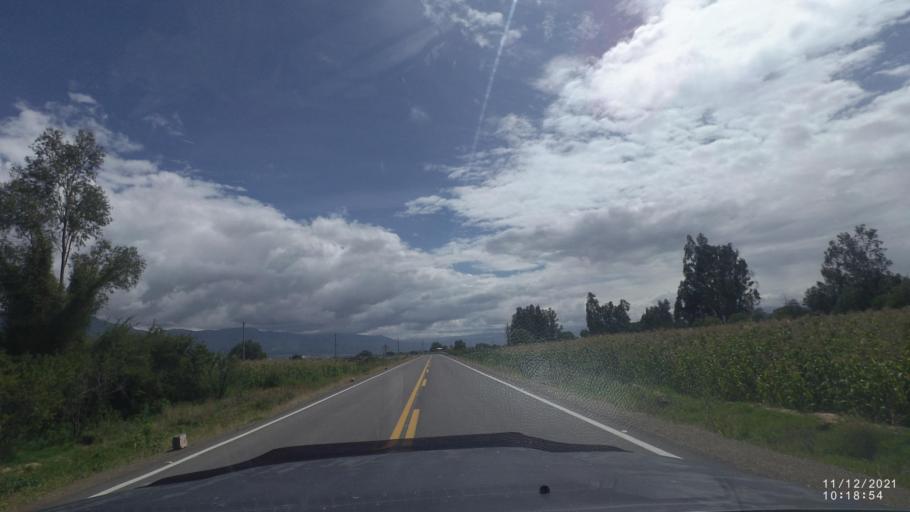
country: BO
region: Cochabamba
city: Tarata
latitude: -17.5753
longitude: -66.0122
